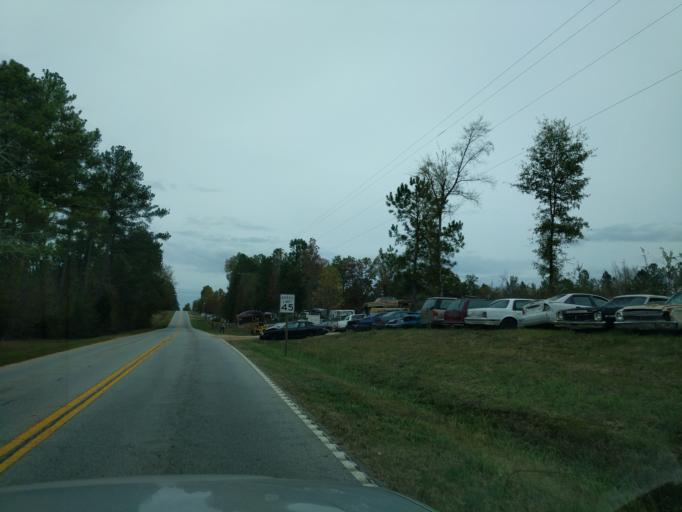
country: US
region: South Carolina
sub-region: Saluda County
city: Saluda
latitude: 34.0736
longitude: -81.7595
